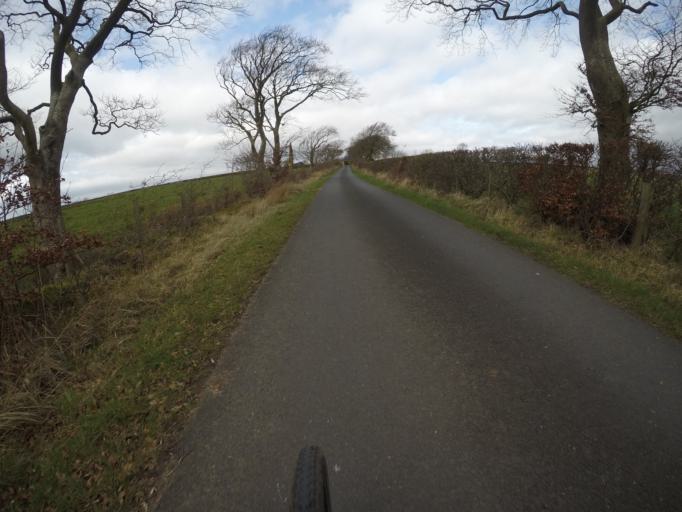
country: GB
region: Scotland
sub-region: North Ayrshire
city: Springside
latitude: 55.6645
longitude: -4.5911
